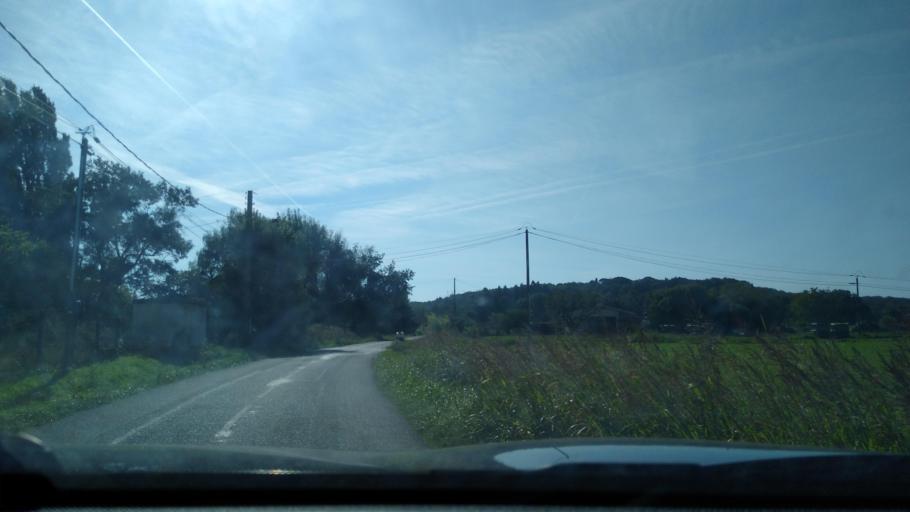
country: FR
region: Midi-Pyrenees
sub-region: Departement de la Haute-Garonne
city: Grenade
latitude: 43.7544
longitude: 1.2563
